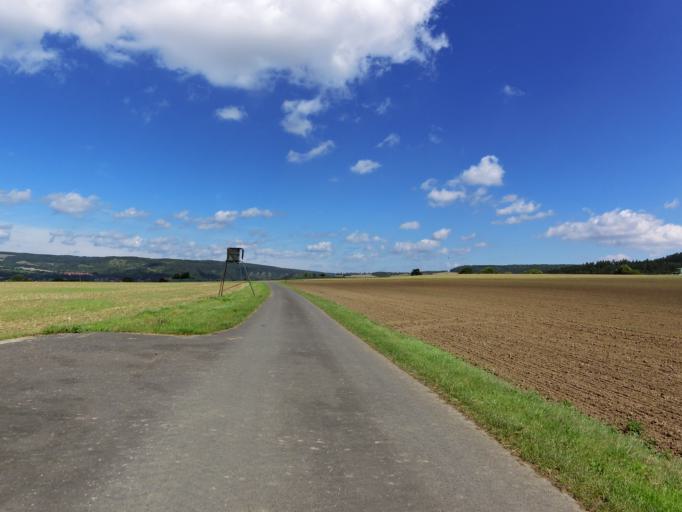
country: DE
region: Thuringia
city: Krauthausen
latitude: 51.0258
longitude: 10.2467
